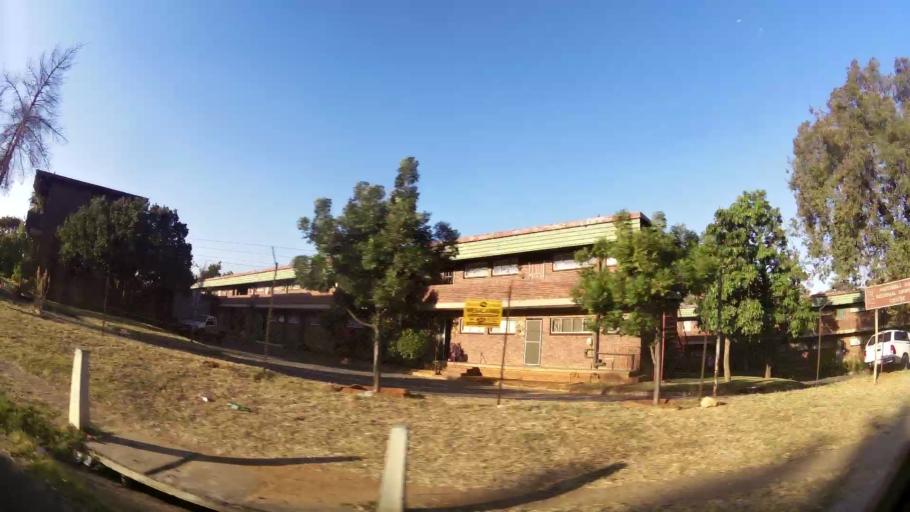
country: ZA
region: North-West
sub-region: Bojanala Platinum District Municipality
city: Rustenburg
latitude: -25.6752
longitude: 27.2126
